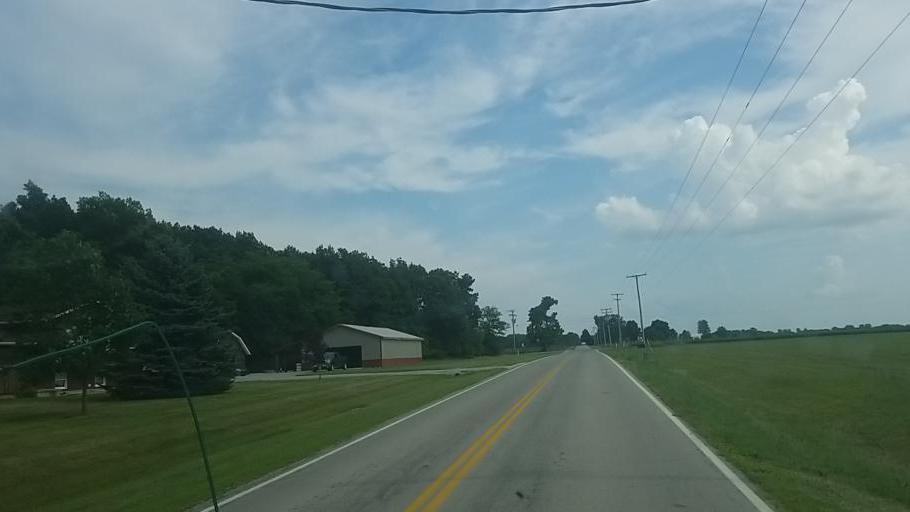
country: US
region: Ohio
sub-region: Wyandot County
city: Upper Sandusky
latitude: 40.7903
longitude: -83.2760
